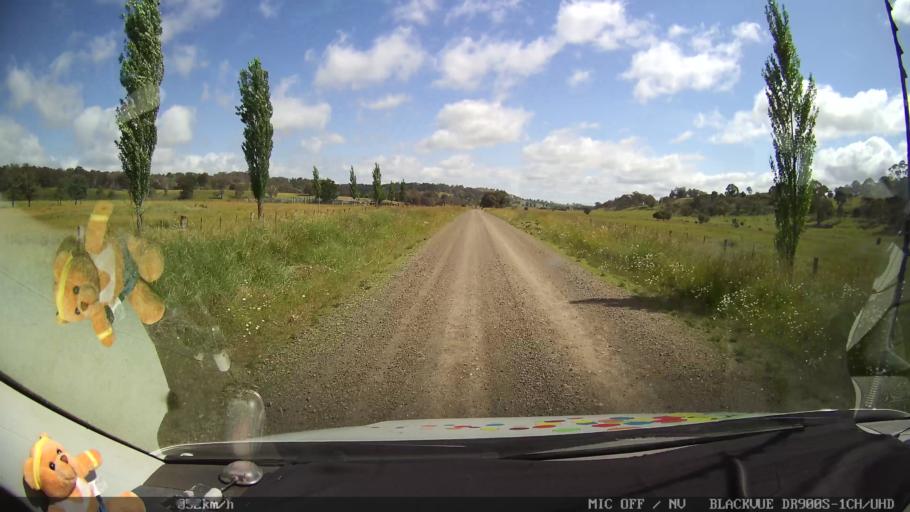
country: AU
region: New South Wales
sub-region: Glen Innes Severn
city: Glen Innes
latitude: -29.9721
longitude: 151.6993
